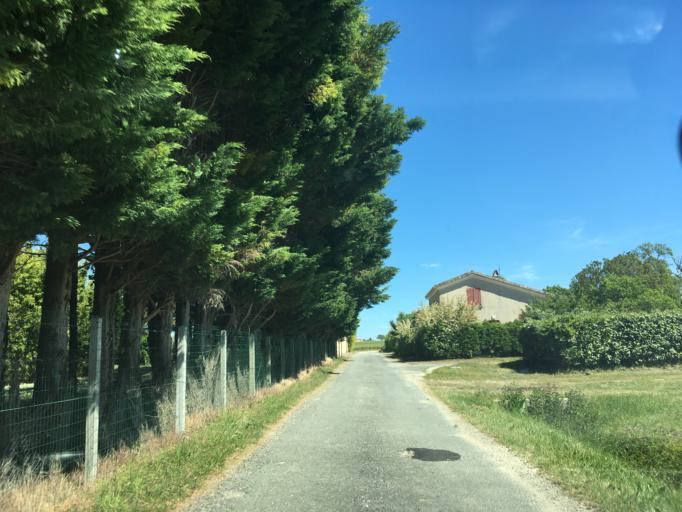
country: FR
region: Aquitaine
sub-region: Departement de la Gironde
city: Lesparre-Medoc
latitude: 45.3147
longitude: -0.8789
